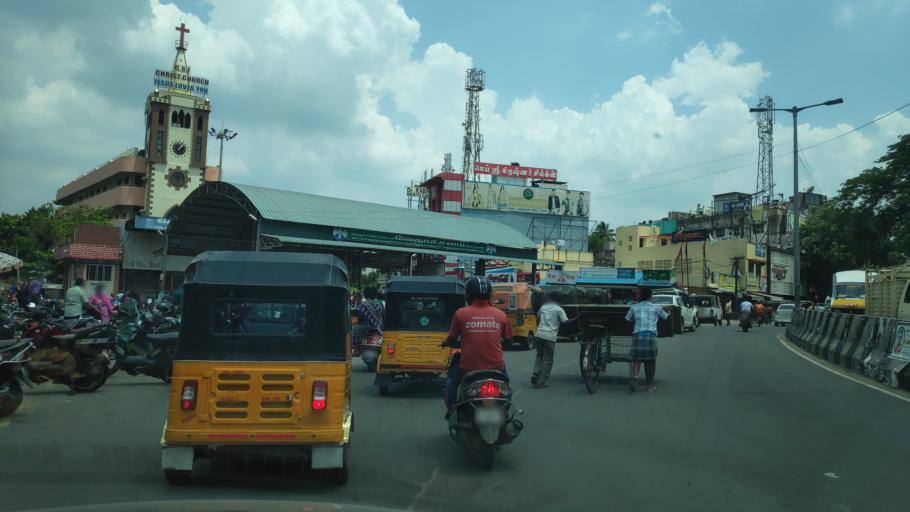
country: IN
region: Tamil Nadu
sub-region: Thiruvallur
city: Ambattur
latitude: 13.1200
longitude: 80.1498
